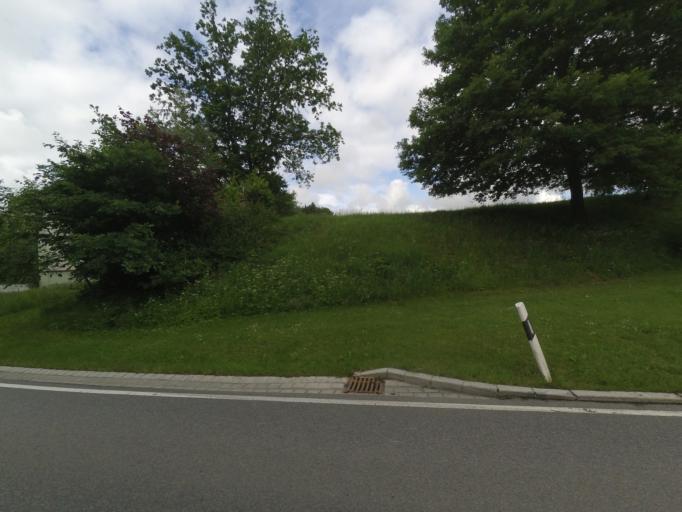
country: DE
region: Bavaria
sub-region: Lower Bavaria
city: Konzell
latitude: 49.0540
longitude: 12.7144
